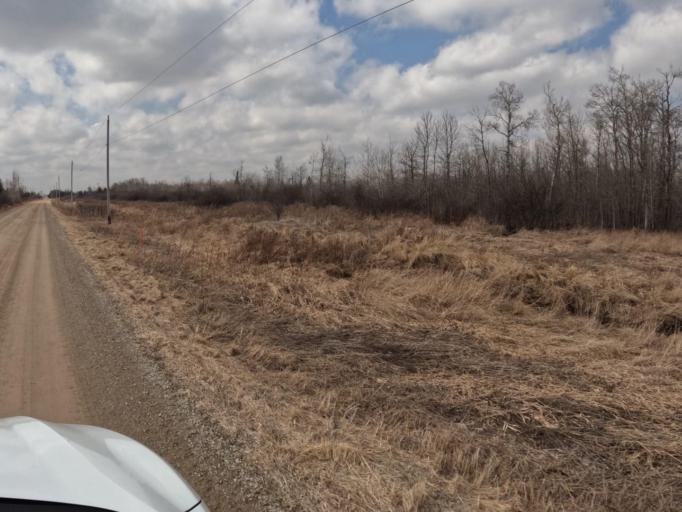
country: CA
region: Ontario
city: Shelburne
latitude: 44.0201
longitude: -80.2992
